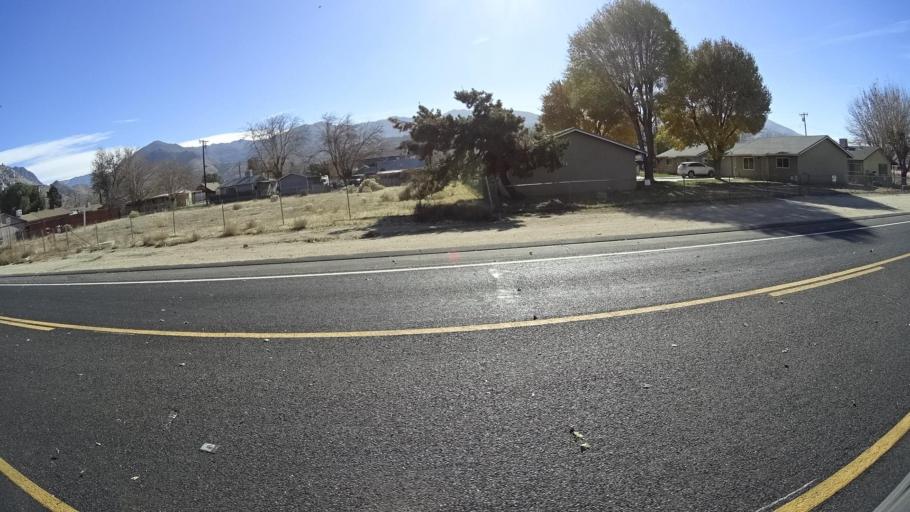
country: US
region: California
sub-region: Kern County
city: Lake Isabella
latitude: 35.6169
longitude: -118.4764
